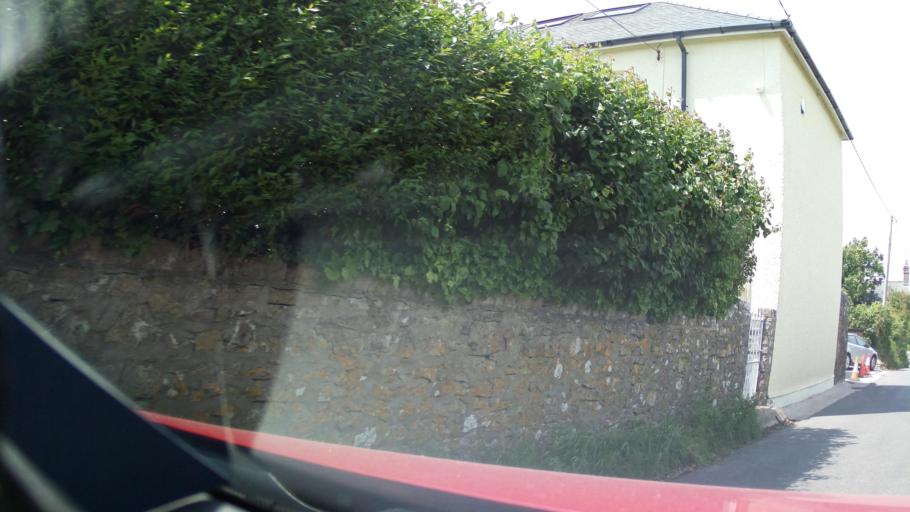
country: GB
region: Wales
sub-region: Vale of Glamorgan
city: Wick
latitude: 51.4251
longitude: -3.5548
